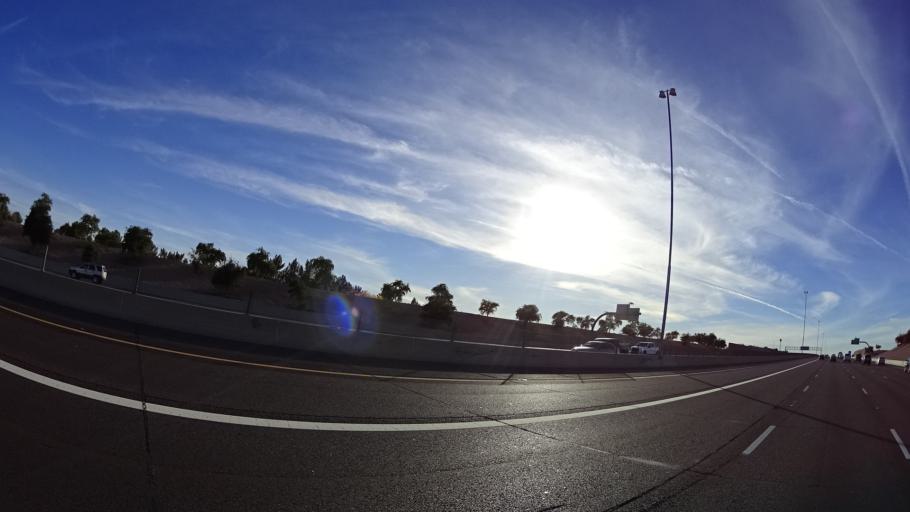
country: US
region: Arizona
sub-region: Maricopa County
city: Gilbert
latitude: 33.3866
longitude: -111.7650
